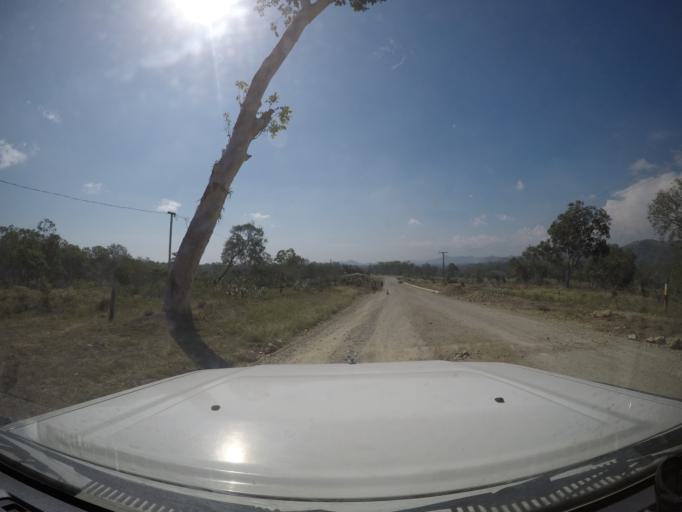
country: PG
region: Central Province
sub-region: Rigo
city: Kwikila
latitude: -9.9608
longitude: 147.6569
